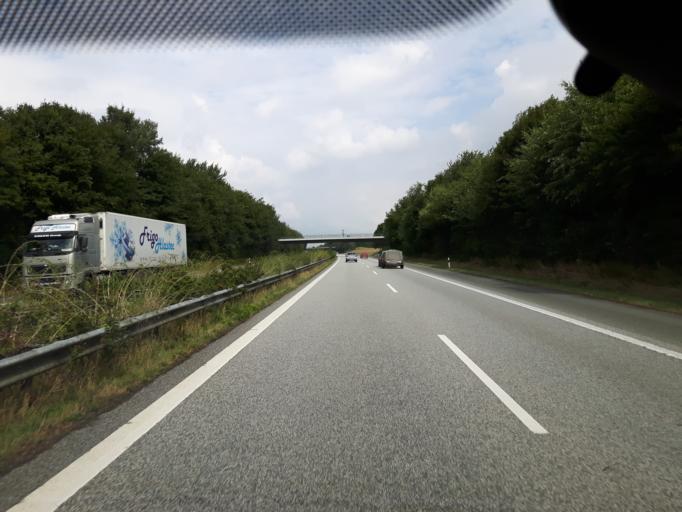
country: DE
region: Schleswig-Holstein
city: Lurschau
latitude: 54.5706
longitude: 9.4694
